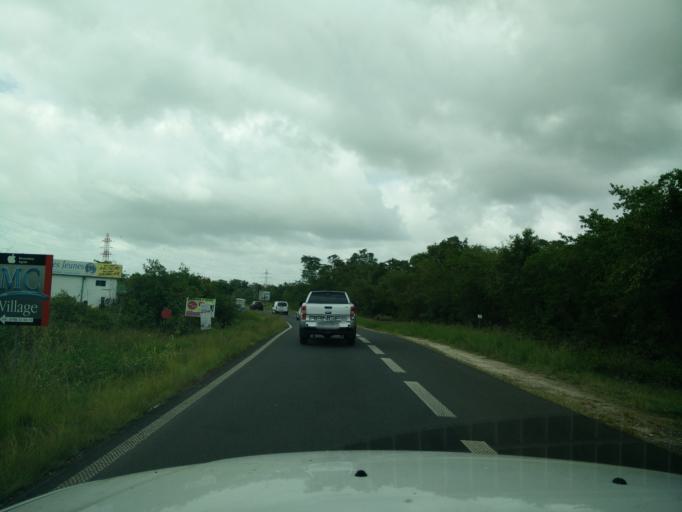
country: GP
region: Guadeloupe
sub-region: Guadeloupe
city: Pointe-a-Pitre
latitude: 16.2521
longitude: -61.5526
